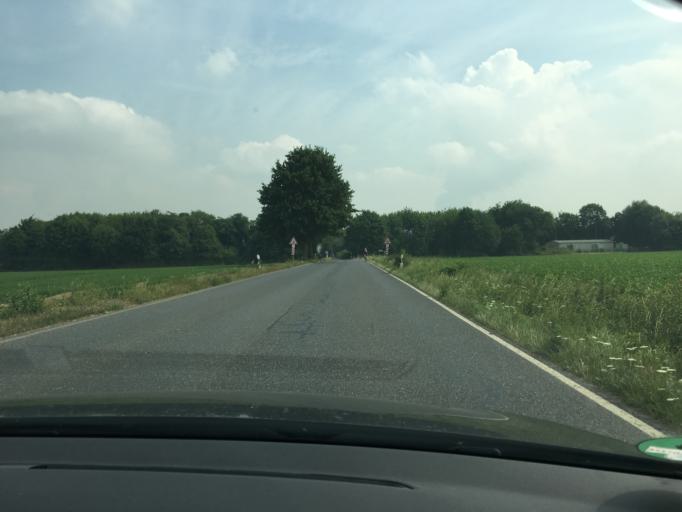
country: DE
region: North Rhine-Westphalia
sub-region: Regierungsbezirk Koln
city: Elsdorf
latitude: 50.9628
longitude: 6.5976
